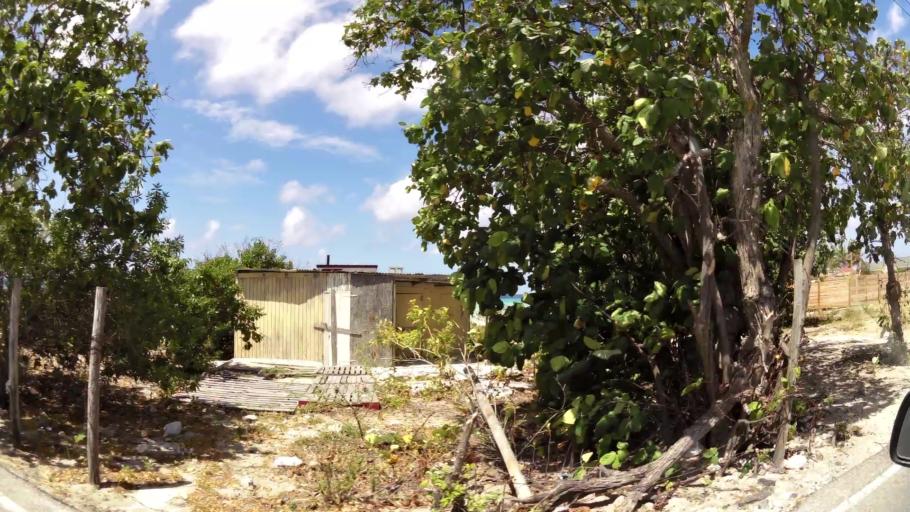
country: TC
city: Cockburn Town
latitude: 21.4758
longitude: -71.1485
